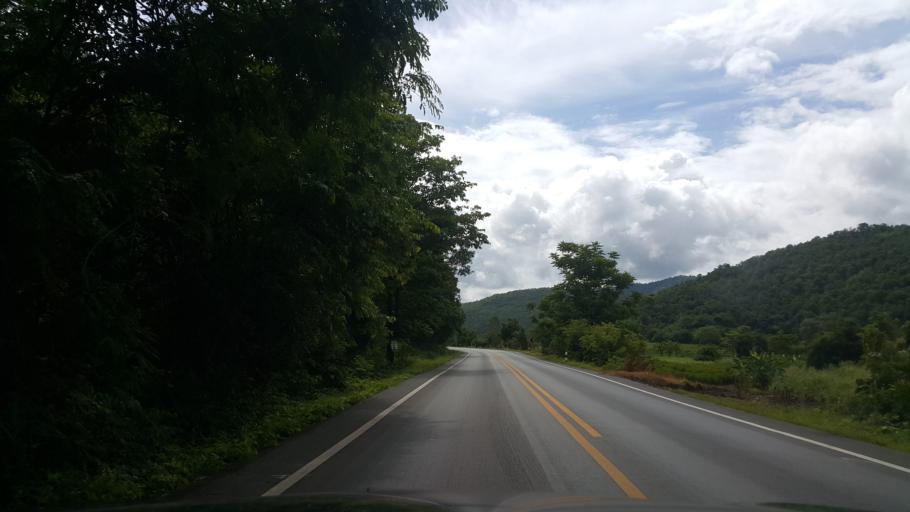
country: TH
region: Uttaradit
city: Thong Saen Khan
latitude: 17.3799
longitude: 100.2795
